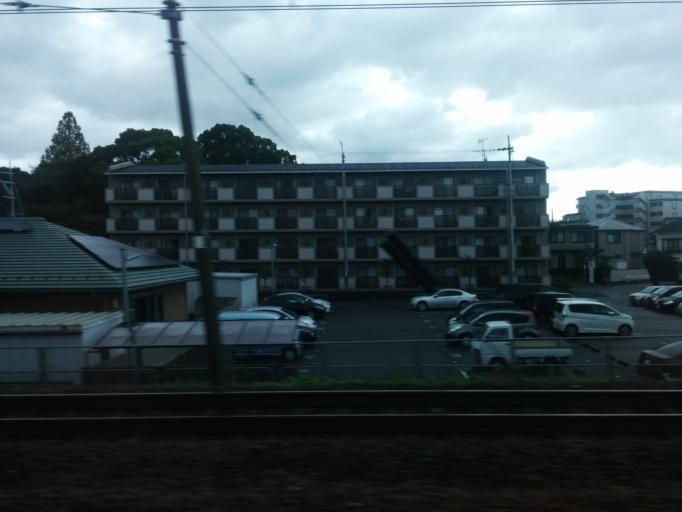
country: JP
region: Shiga Prefecture
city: Kusatsu
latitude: 35.0137
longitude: 135.9548
